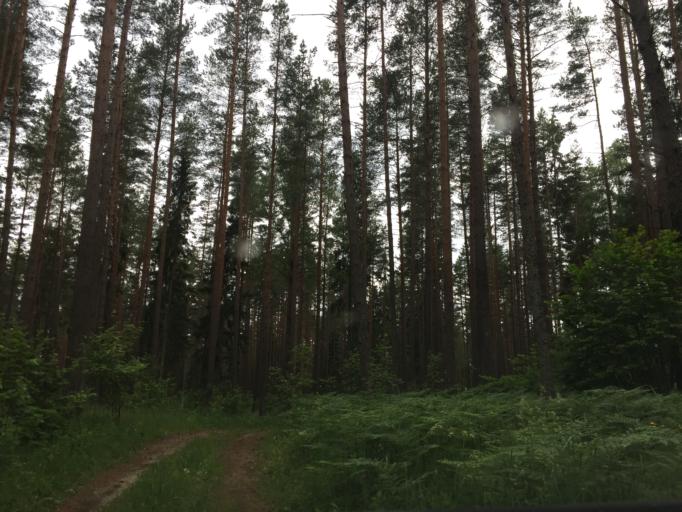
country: LV
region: Tukuma Rajons
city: Tukums
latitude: 57.0279
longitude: 23.0776
